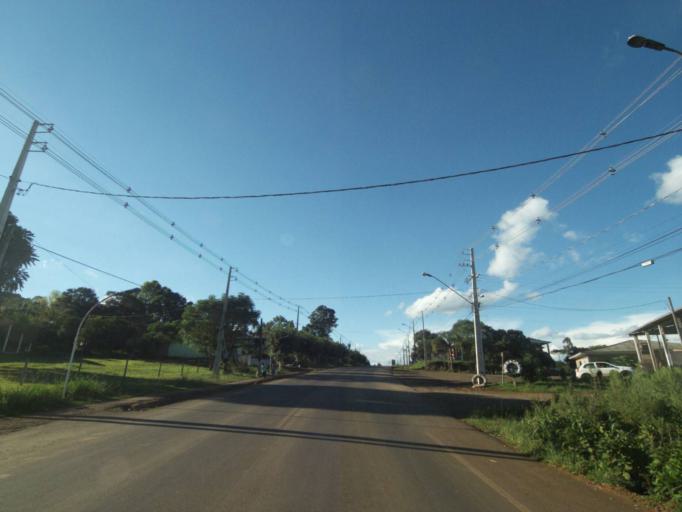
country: BR
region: Parana
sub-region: Uniao Da Vitoria
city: Uniao da Vitoria
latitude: -26.1656
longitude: -51.5357
